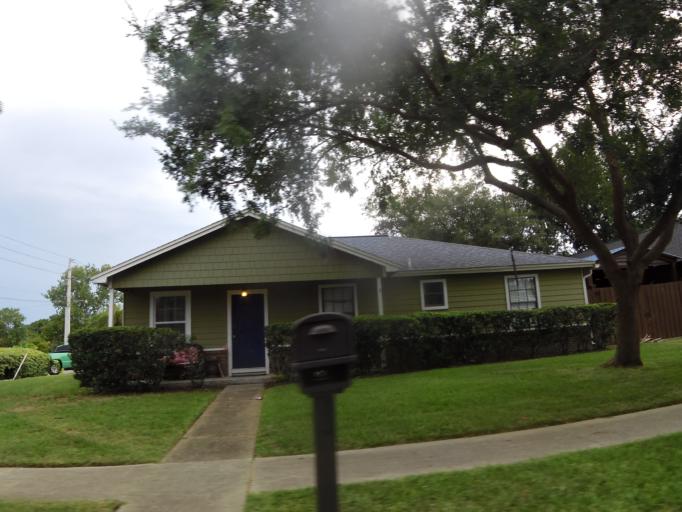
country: US
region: Florida
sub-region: Duval County
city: Jacksonville Beach
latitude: 30.2712
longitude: -81.4006
